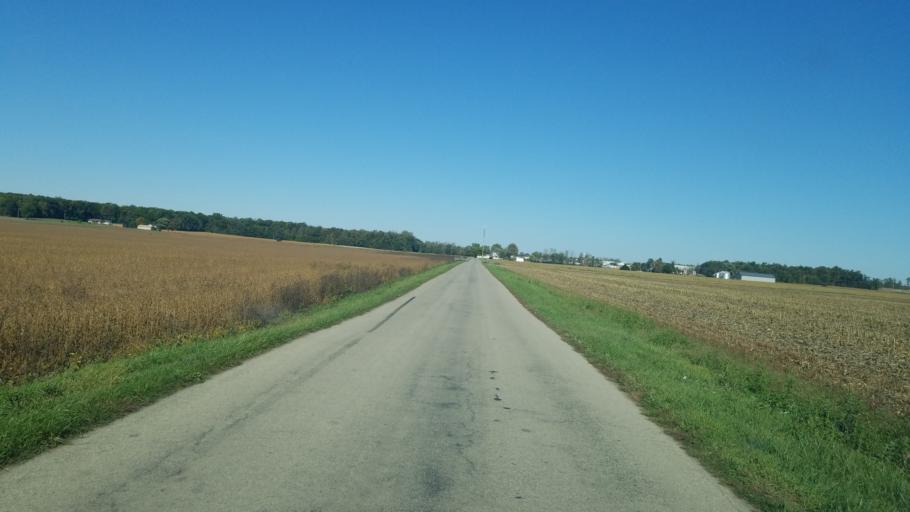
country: US
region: Ohio
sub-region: Huron County
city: Willard
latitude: 41.0245
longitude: -82.7178
